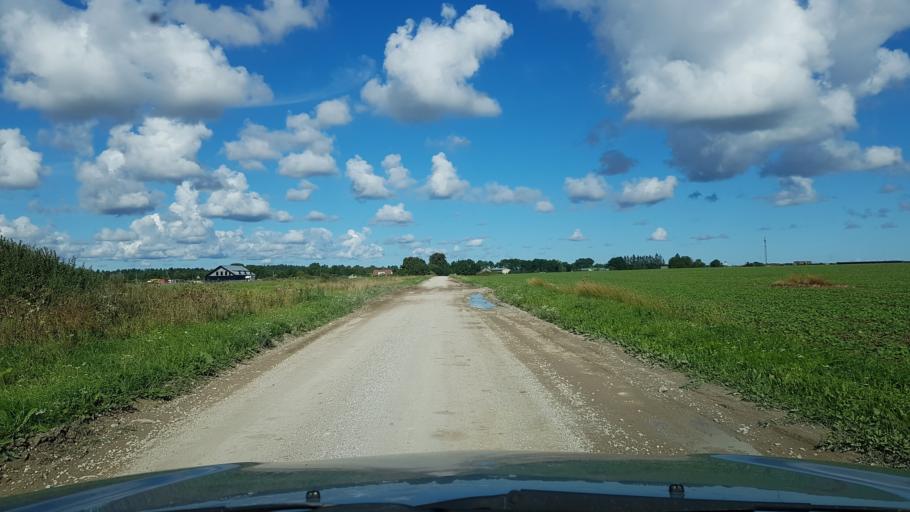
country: EE
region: Harju
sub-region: Kiili vald
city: Kiili
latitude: 59.3751
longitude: 24.8066
